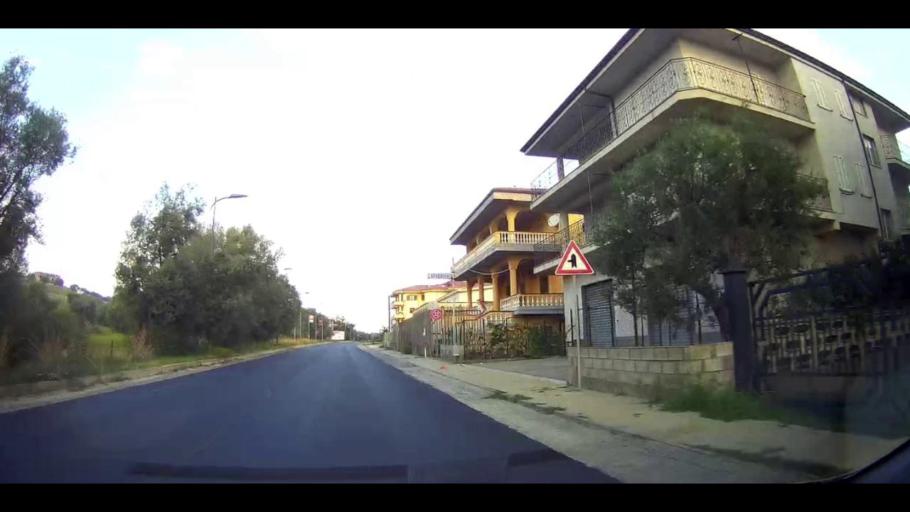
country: IT
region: Calabria
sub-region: Provincia di Crotone
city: Torretta
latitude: 39.4595
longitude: 17.0301
